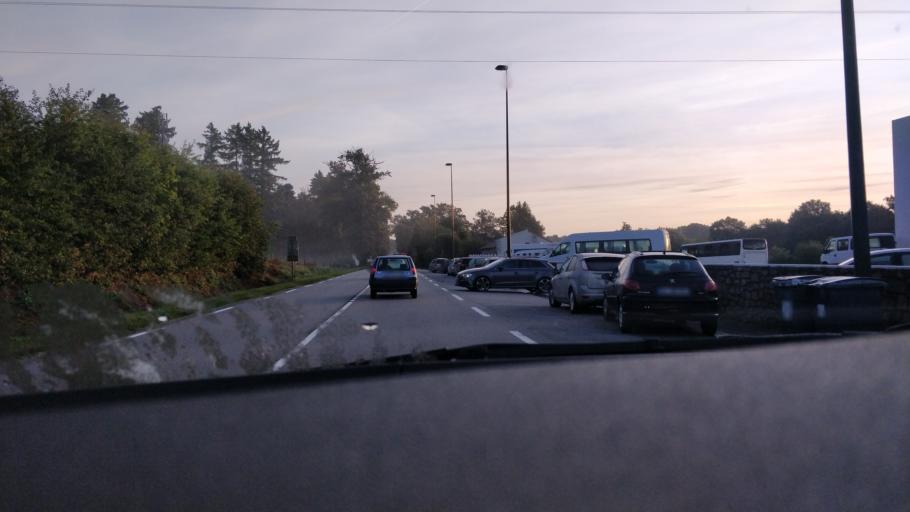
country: FR
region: Limousin
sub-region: Departement de la Haute-Vienne
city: Panazol
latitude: 45.8371
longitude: 1.3210
